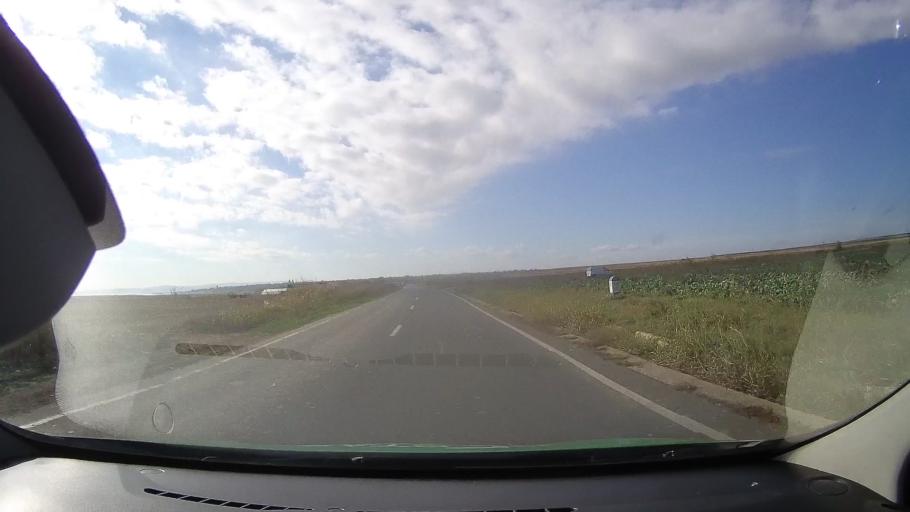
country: RO
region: Tulcea
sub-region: Comuna Sarichioi
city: Sarichioi
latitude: 44.9659
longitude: 28.8650
